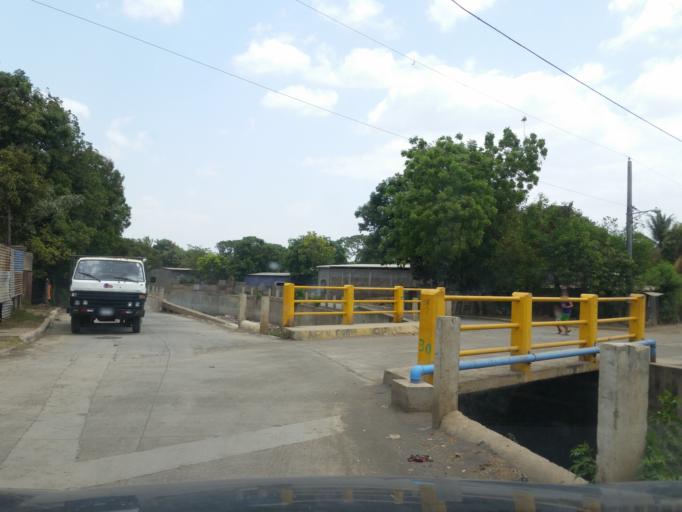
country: NI
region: Managua
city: Managua
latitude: 12.1344
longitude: -86.1903
